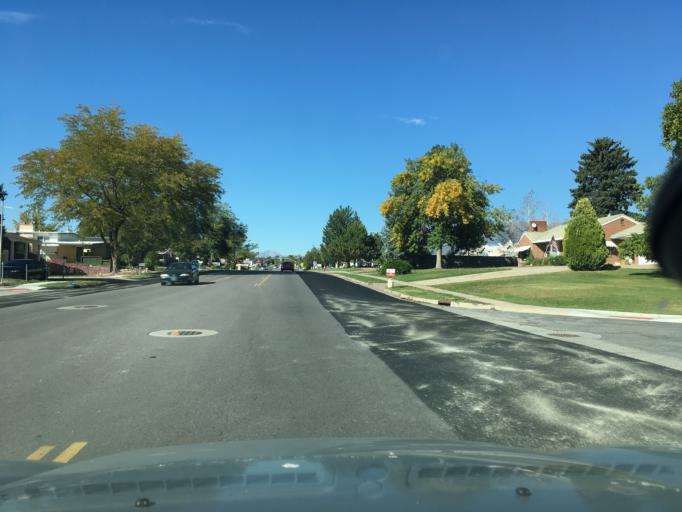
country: US
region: Utah
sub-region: Davis County
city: Layton
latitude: 41.0709
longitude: -111.9501
